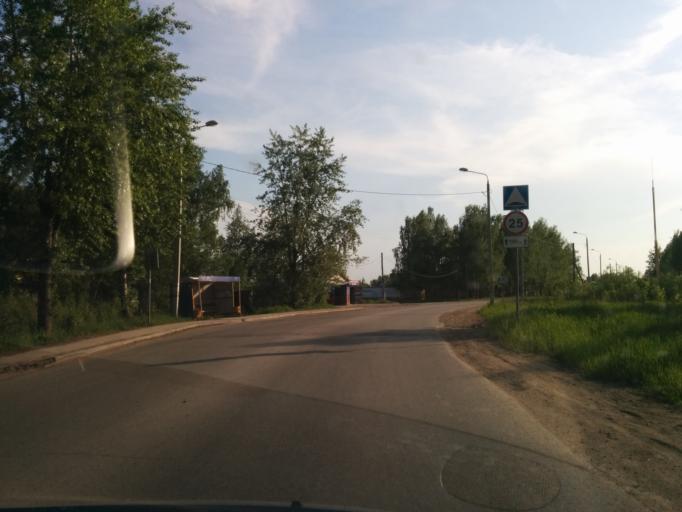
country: RU
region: Perm
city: Perm
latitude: 58.0421
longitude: 56.2706
